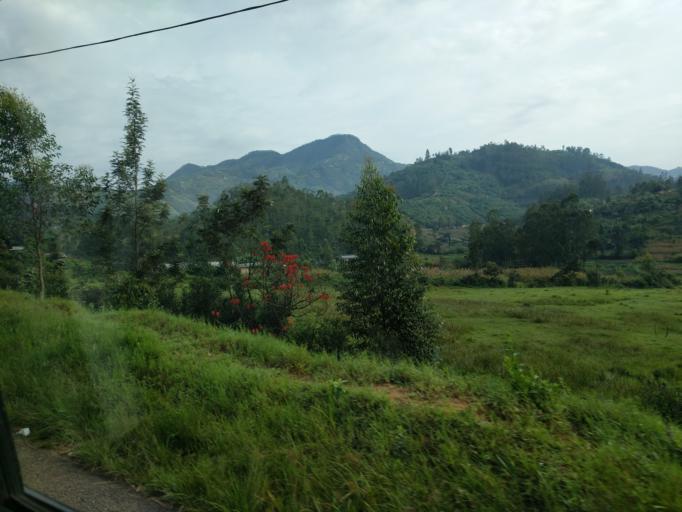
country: RW
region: Northern Province
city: Musanze
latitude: -1.6497
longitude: 29.8048
